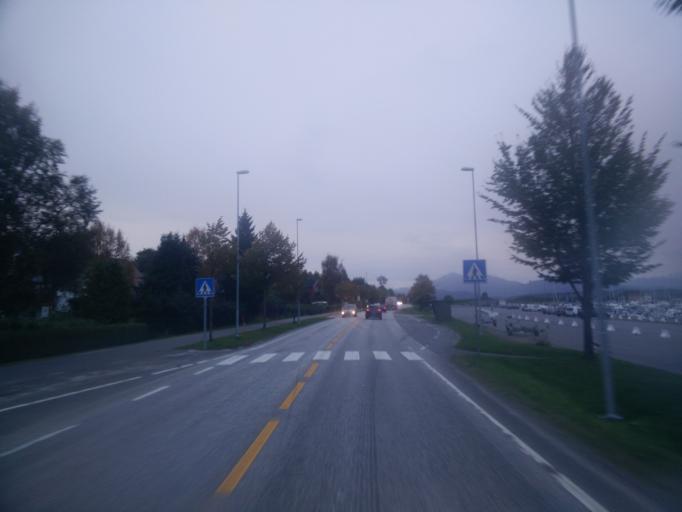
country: NO
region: More og Romsdal
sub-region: Molde
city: Molde
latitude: 62.7402
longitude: 7.2067
